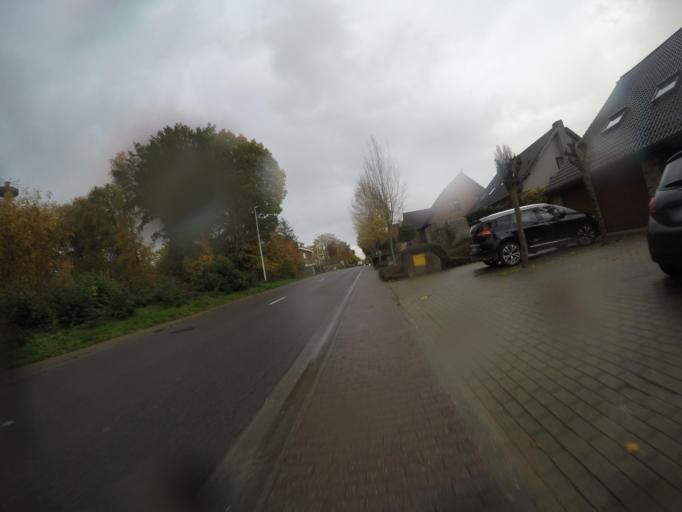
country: BE
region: Flanders
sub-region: Provincie Vlaams-Brabant
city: Liedekerke
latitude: 50.8632
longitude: 4.1076
